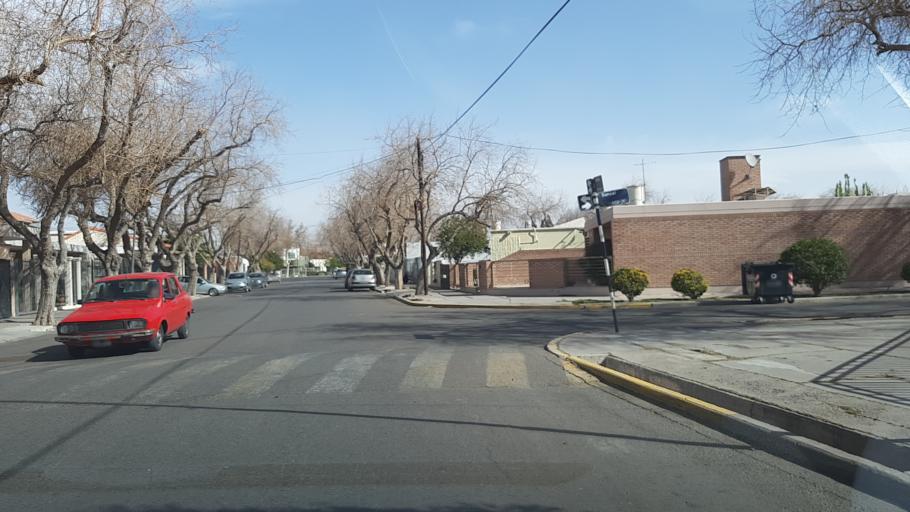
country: AR
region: San Juan
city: San Juan
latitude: -31.5272
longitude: -68.5461
